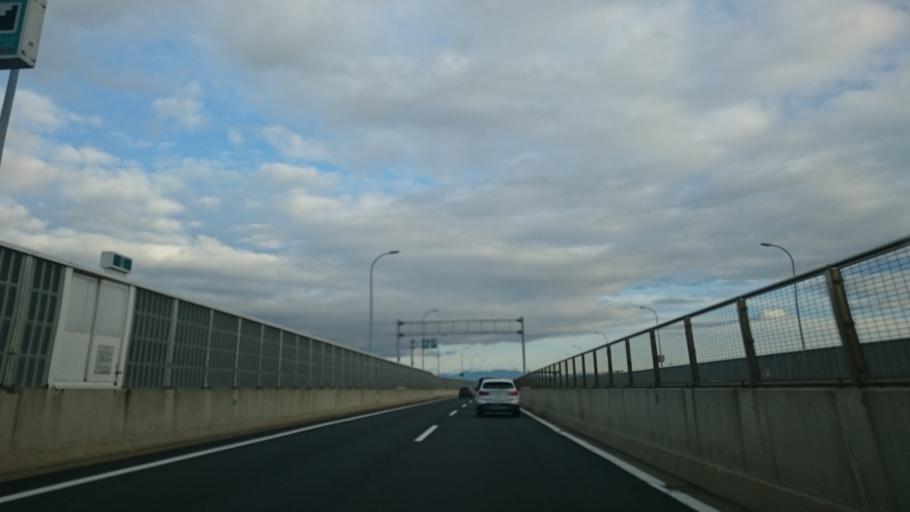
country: JP
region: Aichi
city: Komaki
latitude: 35.2542
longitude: 136.9075
